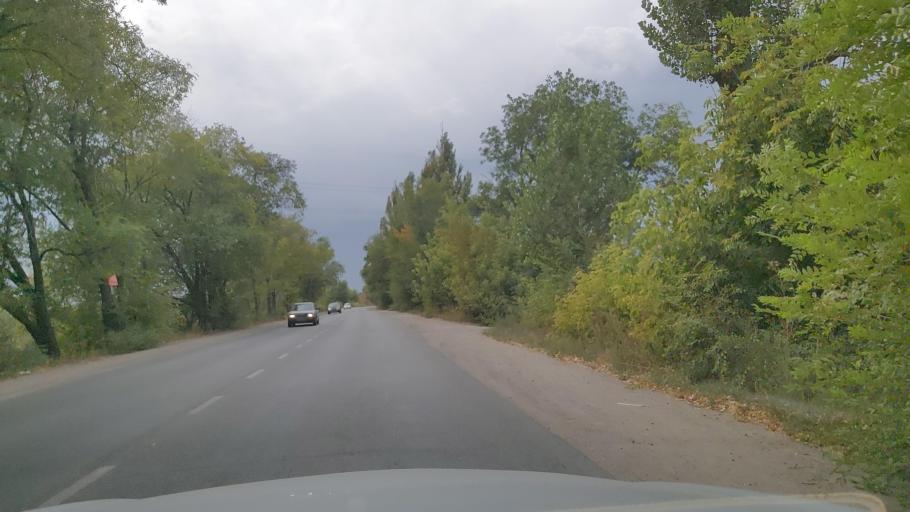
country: KZ
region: Almaty Oblysy
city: Energeticheskiy
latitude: 43.4031
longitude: 77.0362
